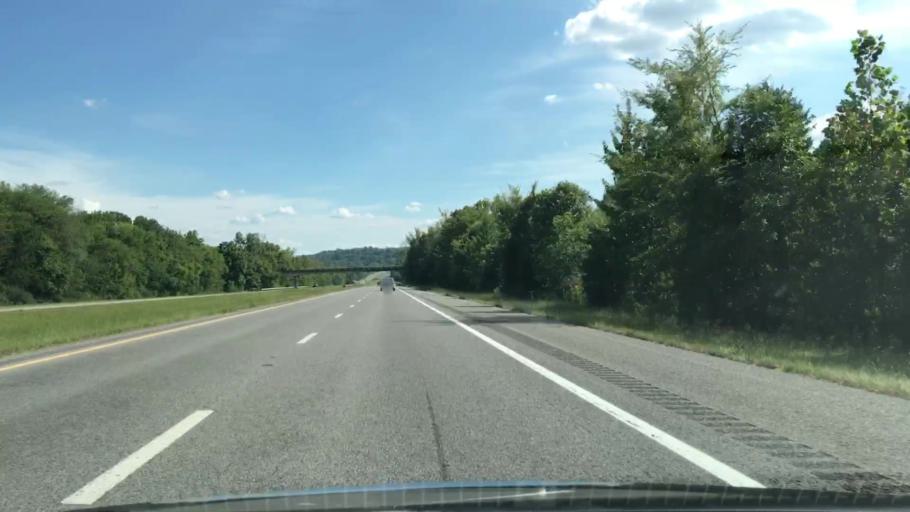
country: US
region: Alabama
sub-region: Limestone County
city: Ardmore
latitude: 35.1412
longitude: -86.8786
